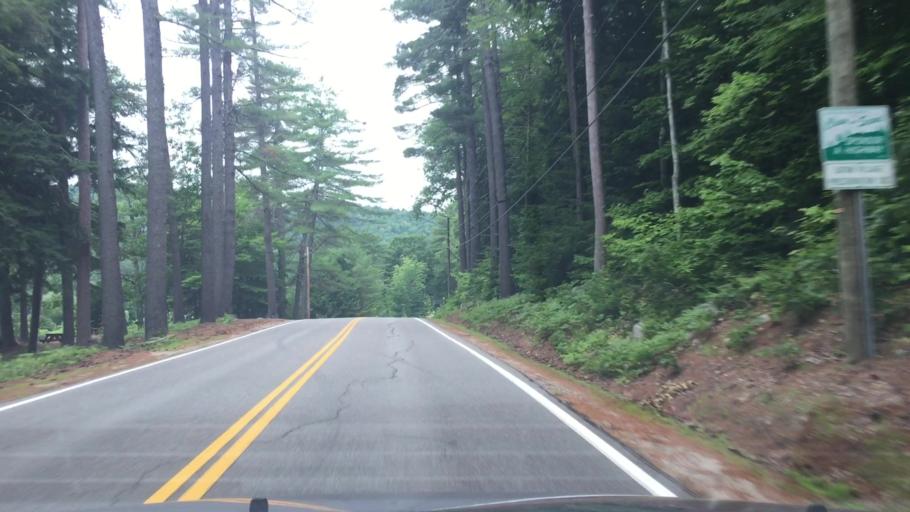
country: US
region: New Hampshire
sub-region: Carroll County
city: Madison
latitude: 43.9138
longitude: -71.0759
